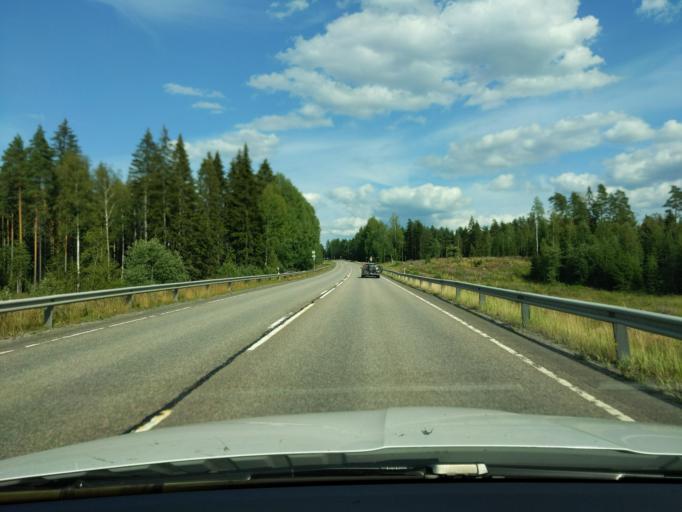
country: FI
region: Kymenlaakso
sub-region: Kouvola
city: Iitti
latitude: 60.9129
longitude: 26.2075
